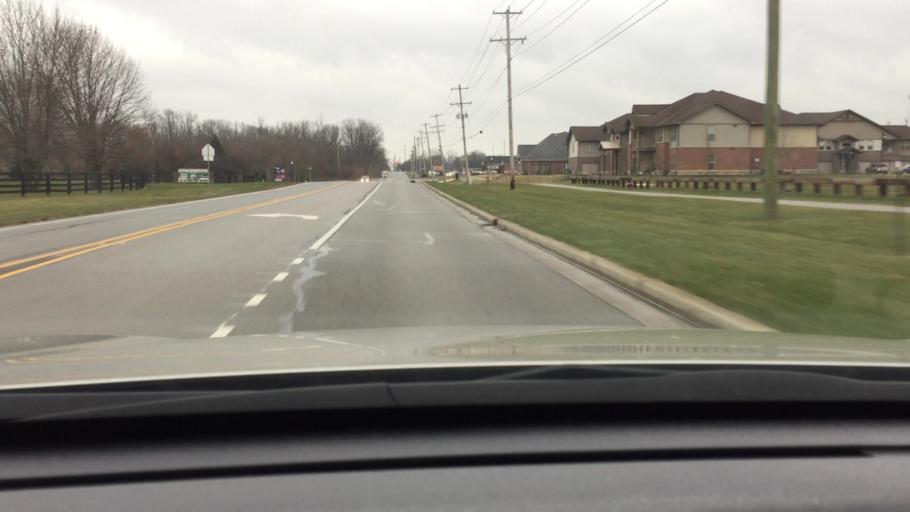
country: US
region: Indiana
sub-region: Hamilton County
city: Carmel
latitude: 40.0064
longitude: -86.0898
